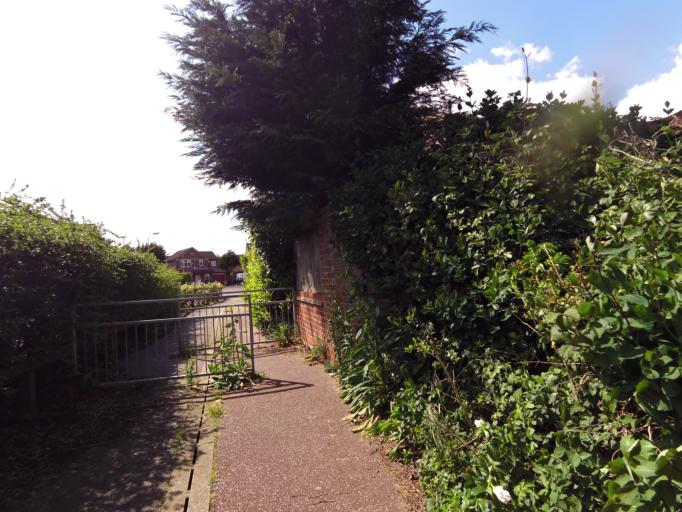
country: GB
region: England
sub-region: Suffolk
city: Kessingland
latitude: 52.4524
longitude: 1.7074
